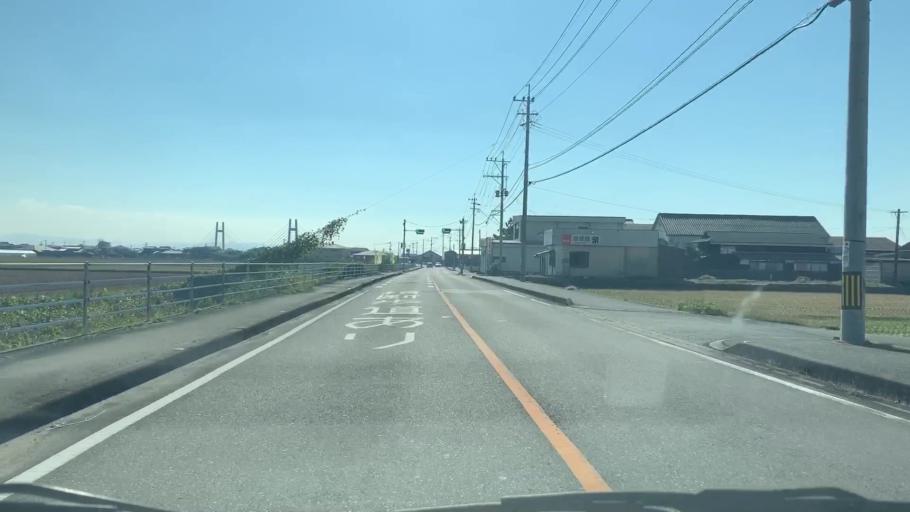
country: JP
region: Saga Prefecture
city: Kanzakimachi-kanzaki
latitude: 33.2933
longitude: 130.4452
